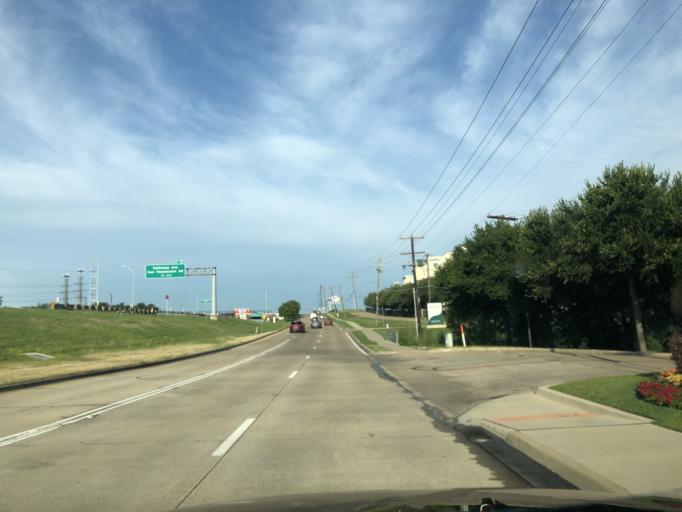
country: US
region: Texas
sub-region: Dallas County
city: Sunnyvale
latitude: 32.8350
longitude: -96.6095
